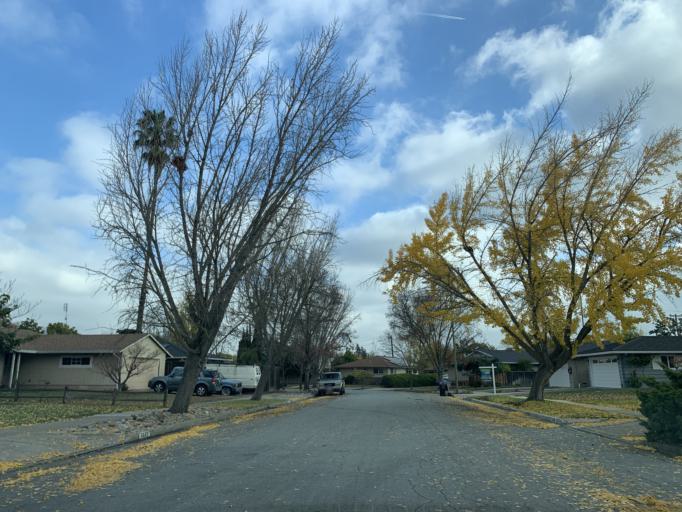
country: US
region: California
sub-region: Santa Clara County
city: Cambrian Park
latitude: 37.2495
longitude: -121.9175
